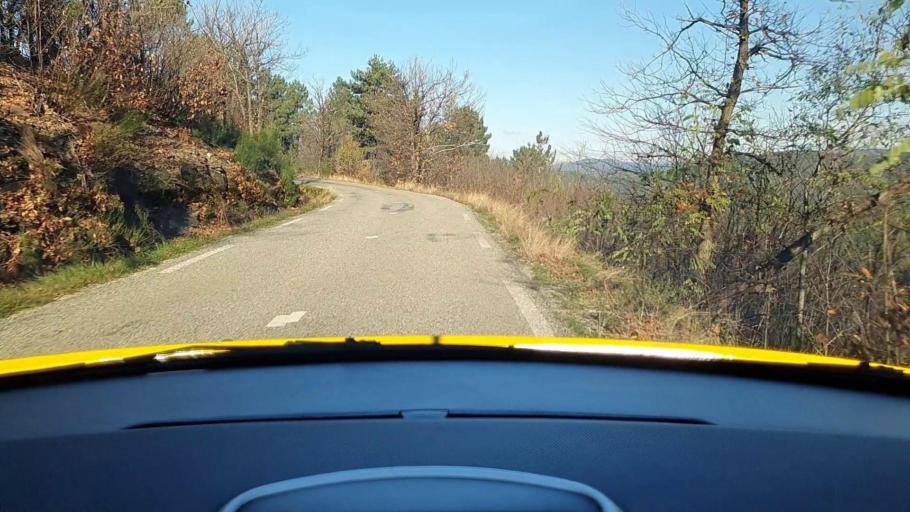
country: FR
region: Languedoc-Roussillon
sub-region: Departement du Gard
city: Branoux-les-Taillades
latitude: 44.2862
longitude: 3.9787
